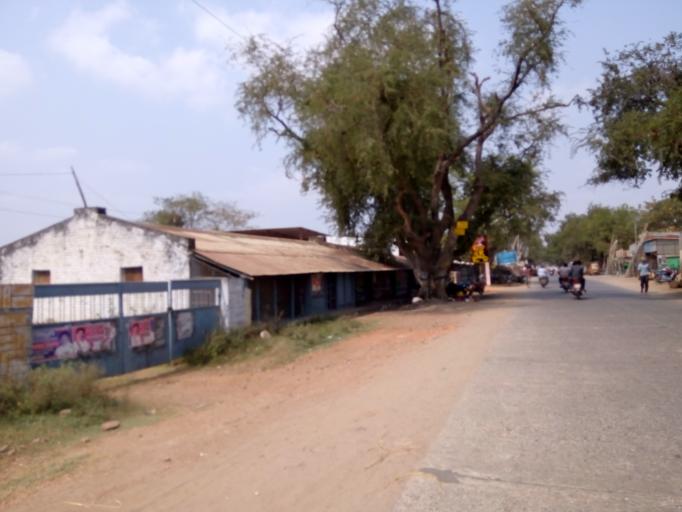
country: IN
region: Andhra Pradesh
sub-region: Prakasam
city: pedda nakkalapalem
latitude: 15.9643
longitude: 80.2783
